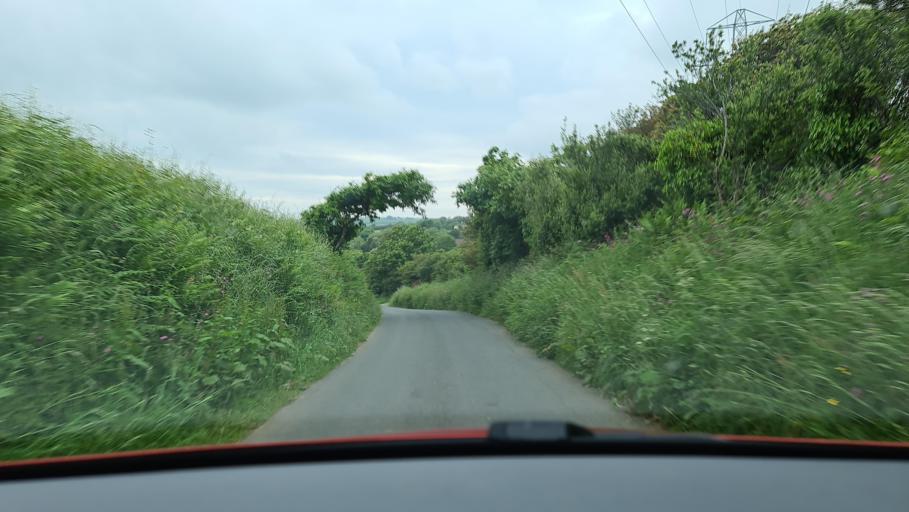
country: GB
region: England
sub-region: Cornwall
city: Camelford
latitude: 50.6165
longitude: -4.6893
